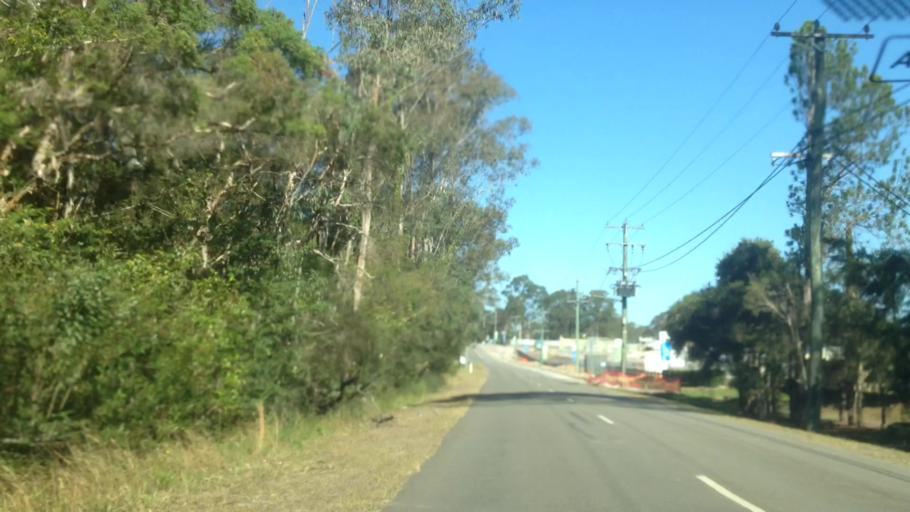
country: AU
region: New South Wales
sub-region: Lake Macquarie Shire
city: Cooranbong
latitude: -33.0901
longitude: 151.4500
